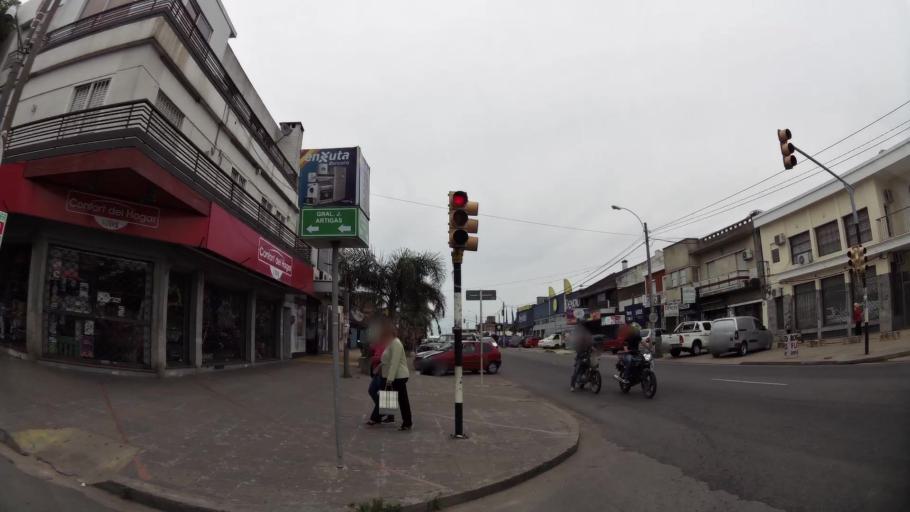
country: UY
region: Canelones
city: Las Piedras
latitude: -34.7272
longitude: -56.2237
